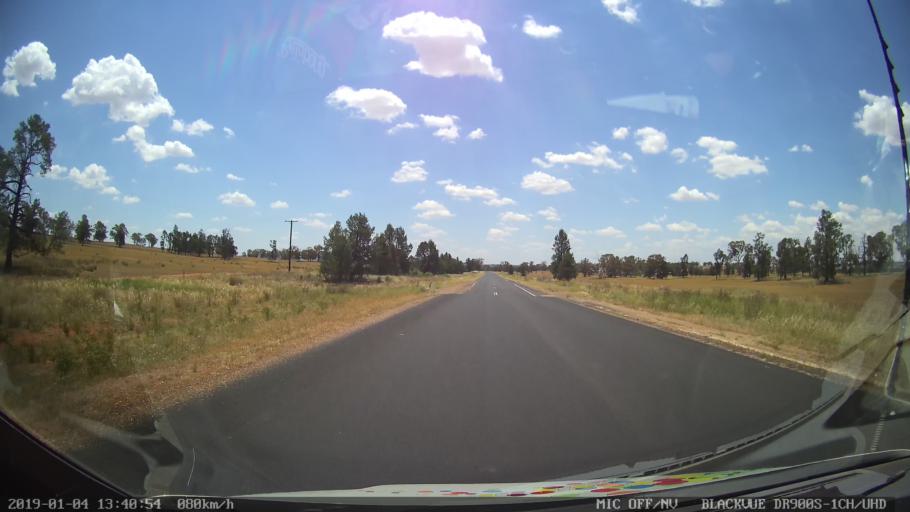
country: AU
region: New South Wales
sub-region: Dubbo Municipality
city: Dubbo
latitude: -32.5090
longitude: 148.5539
